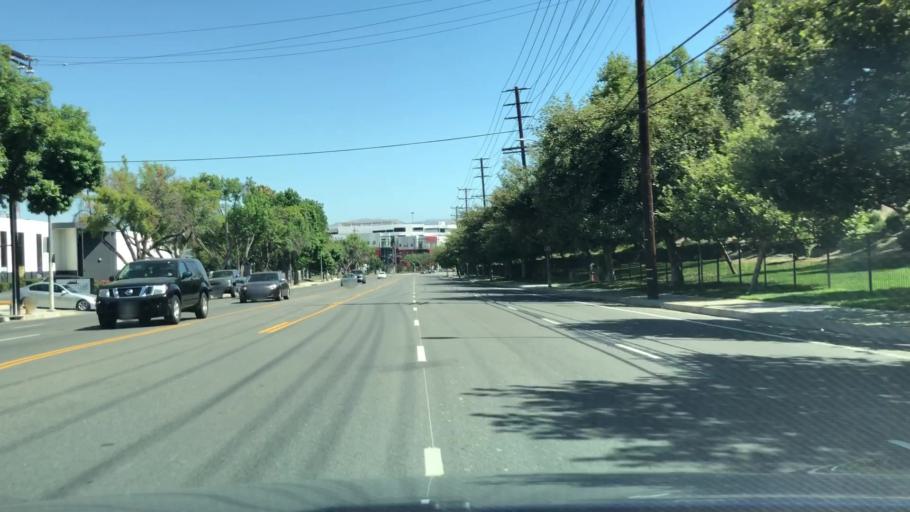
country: US
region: California
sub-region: Los Angeles County
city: Woodland Hills
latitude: 34.1801
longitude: -118.5904
